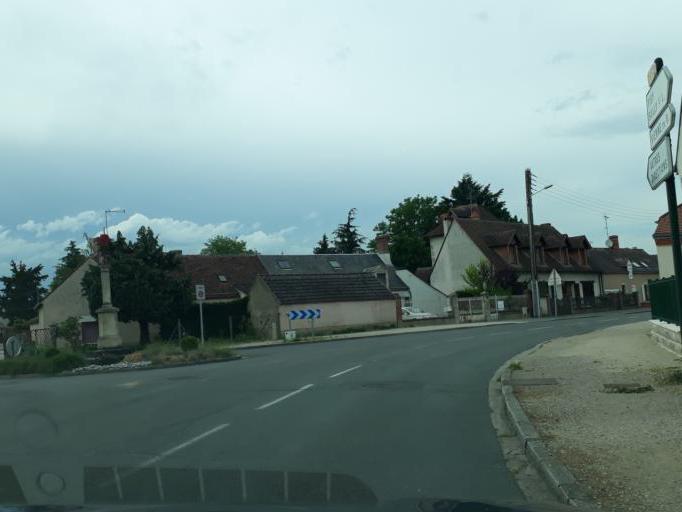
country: FR
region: Centre
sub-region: Departement du Loiret
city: Jargeau
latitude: 47.8601
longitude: 2.1230
